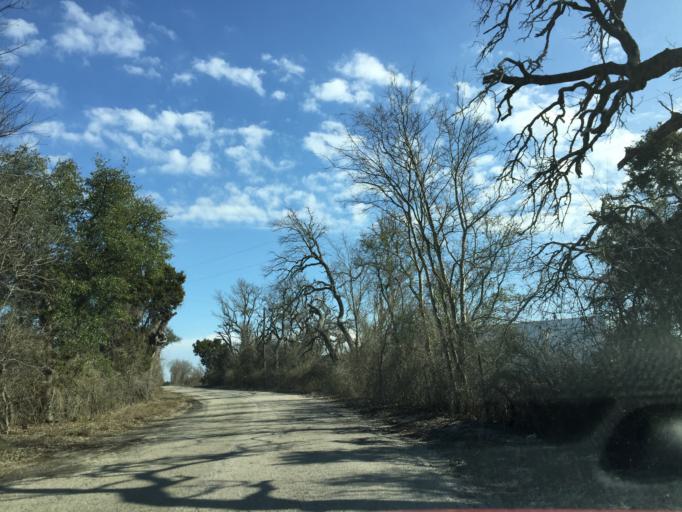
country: US
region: Texas
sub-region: Williamson County
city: Florence
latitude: 30.7834
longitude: -97.8964
